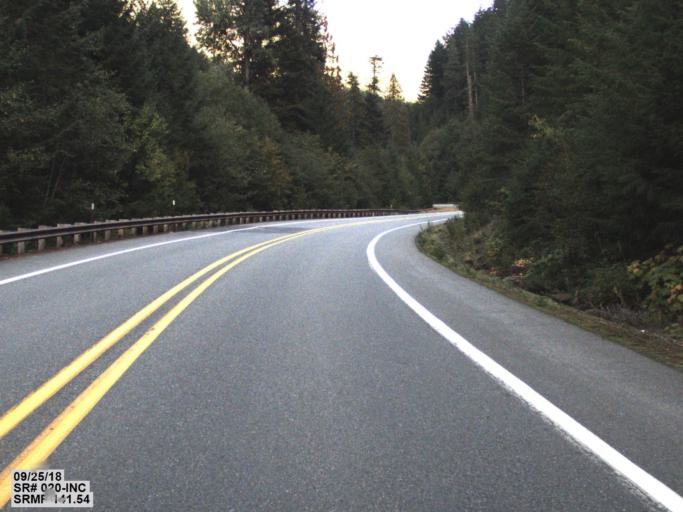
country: US
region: Washington
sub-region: Snohomish County
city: Darrington
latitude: 48.7043
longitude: -120.9128
